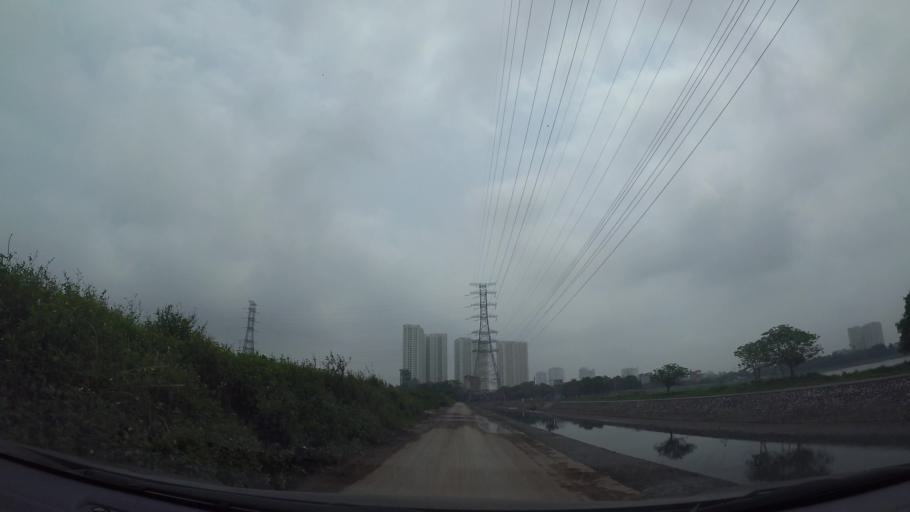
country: VN
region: Ha Noi
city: Van Dien
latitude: 20.9757
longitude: 105.8626
